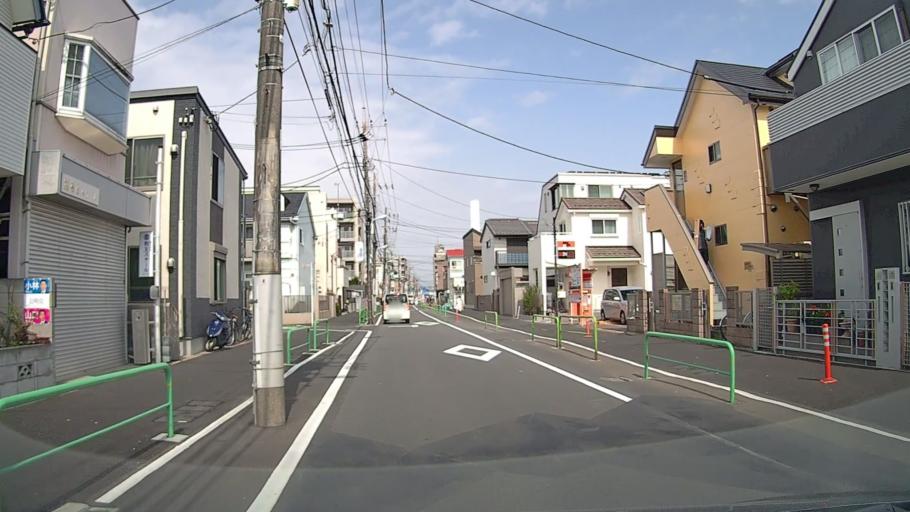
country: JP
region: Saitama
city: Wako
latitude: 35.7513
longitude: 139.6075
